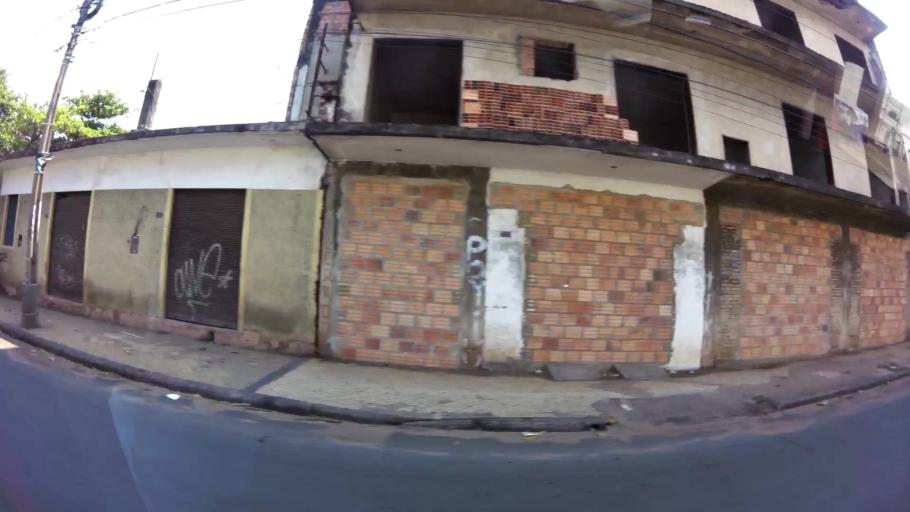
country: PY
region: Asuncion
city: Asuncion
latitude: -25.2925
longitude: -57.6455
